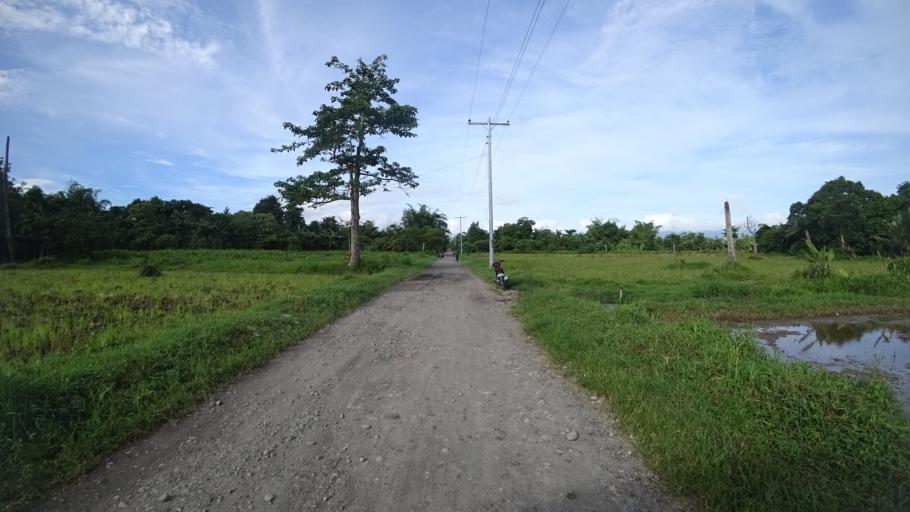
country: PH
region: Eastern Visayas
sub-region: Province of Leyte
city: Pastrana
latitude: 11.1610
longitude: 124.8650
